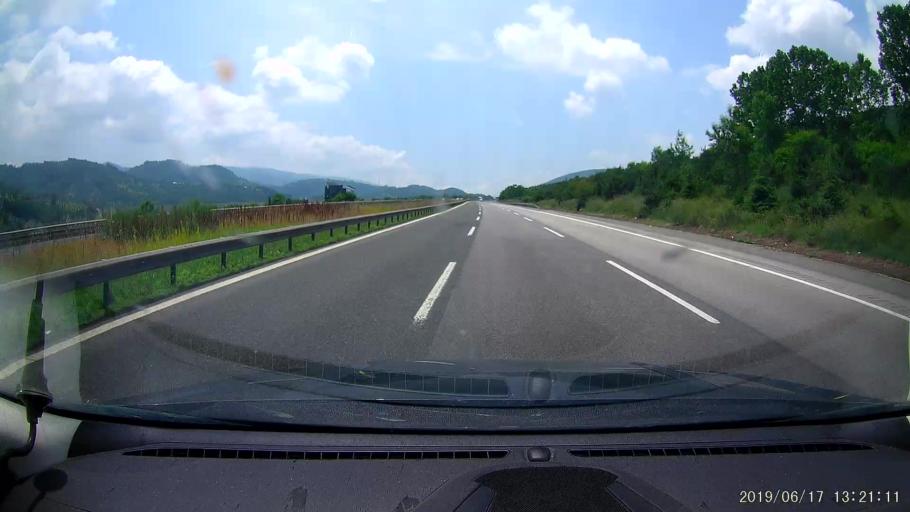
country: TR
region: Duzce
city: Gumusova
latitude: 40.8367
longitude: 30.9407
